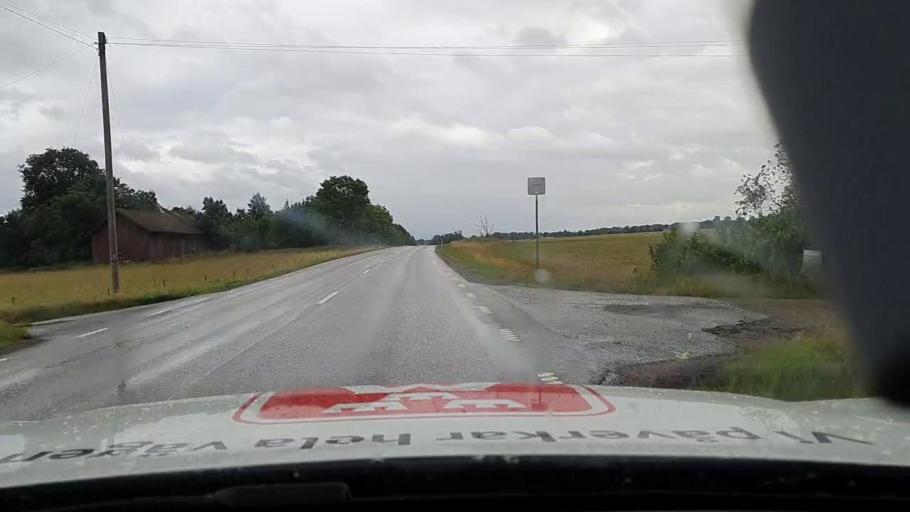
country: SE
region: Vaestra Goetaland
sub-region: Toreboda Kommun
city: Toereboda
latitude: 58.5979
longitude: 14.0097
